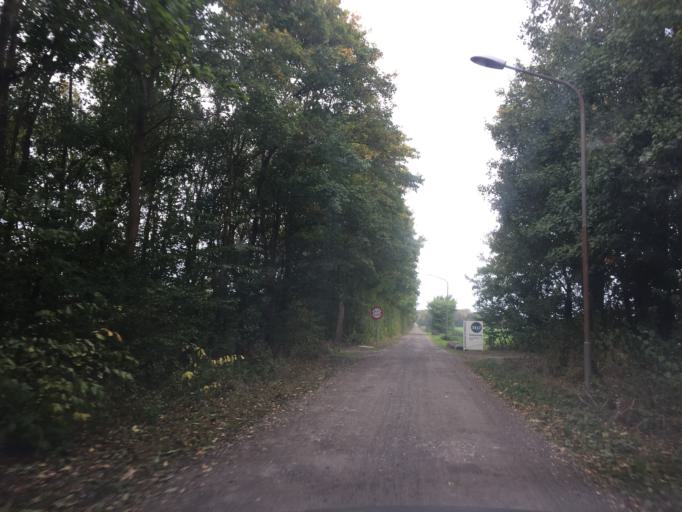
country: DK
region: Zealand
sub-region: Lolland Kommune
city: Rodbyhavn
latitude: 54.6645
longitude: 11.3508
